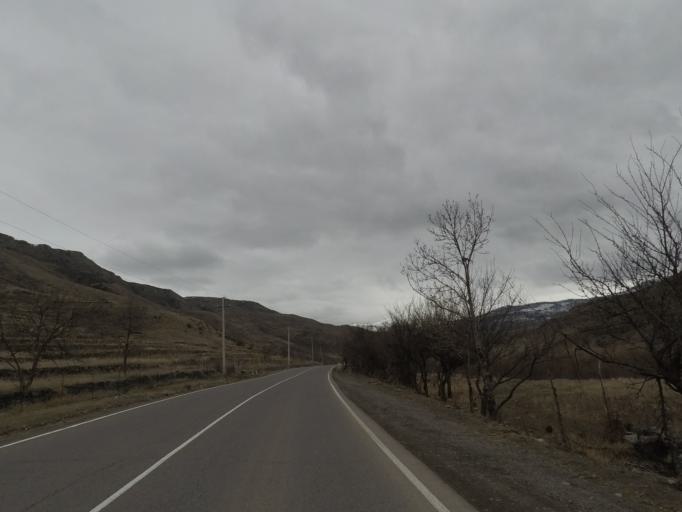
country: GE
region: Samtskhe-Javakheti
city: Aspindza
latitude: 41.5379
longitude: 43.2586
